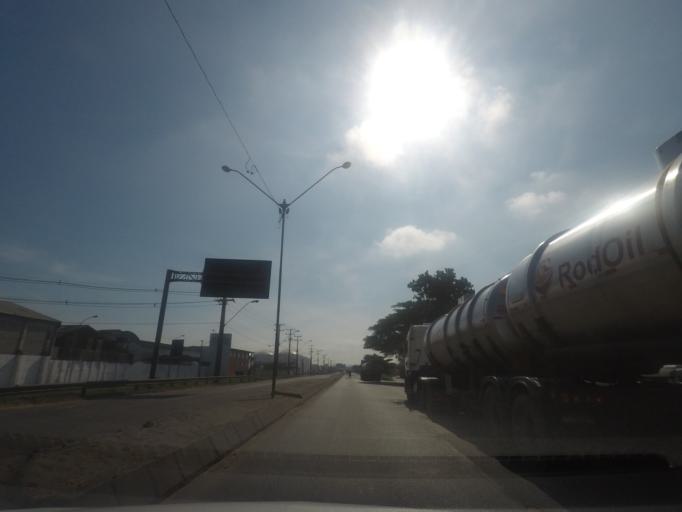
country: BR
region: Parana
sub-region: Paranagua
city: Paranagua
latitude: -25.5224
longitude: -48.5258
